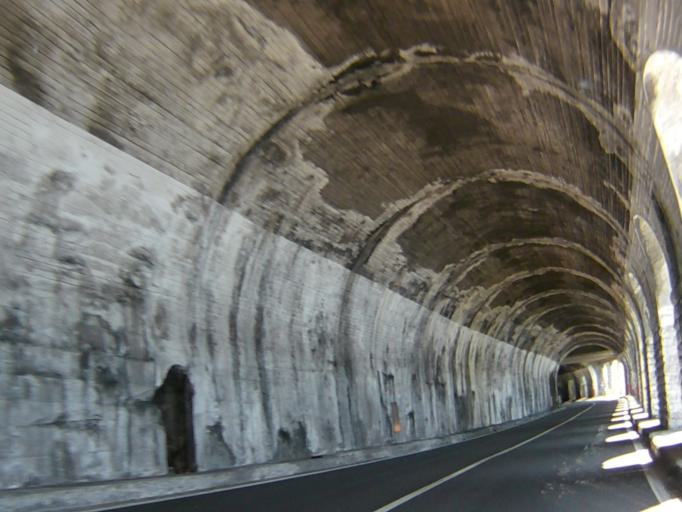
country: IT
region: Lombardy
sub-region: Provincia di Lecco
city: Lierna
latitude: 45.9455
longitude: 9.3064
